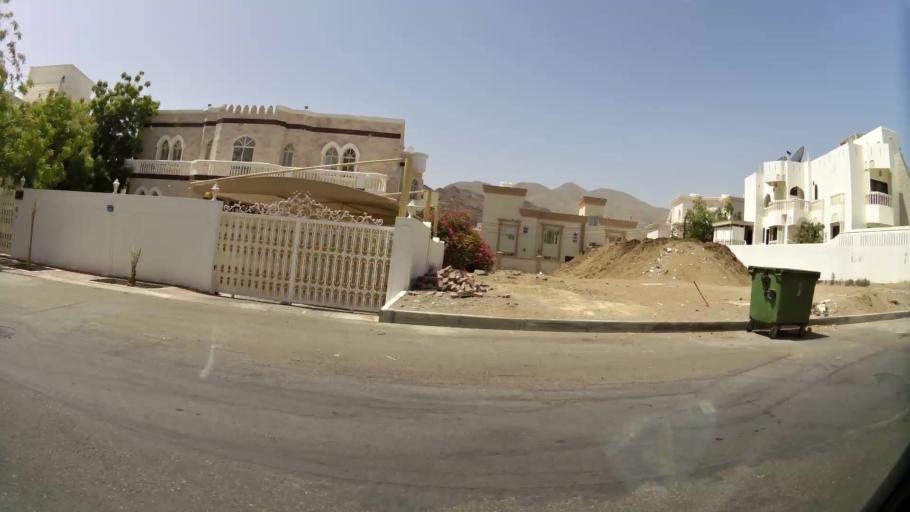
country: OM
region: Muhafazat Masqat
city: Bawshar
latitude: 23.5915
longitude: 58.4551
